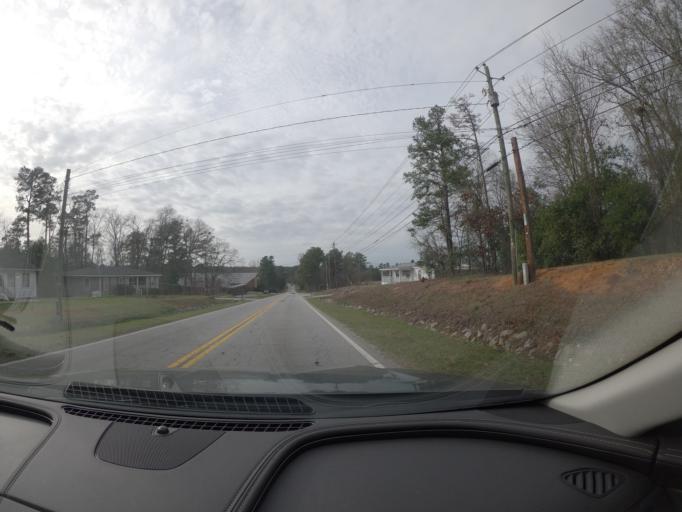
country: US
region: Georgia
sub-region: Columbia County
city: Evans
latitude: 33.4752
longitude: -82.1333
